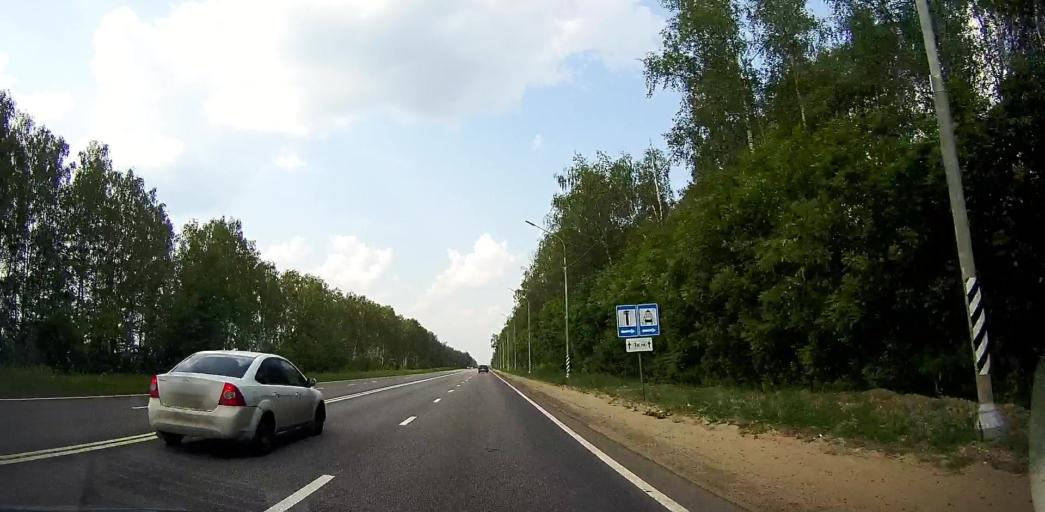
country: RU
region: Moskovskaya
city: Mikhnevo
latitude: 55.0978
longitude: 37.9498
